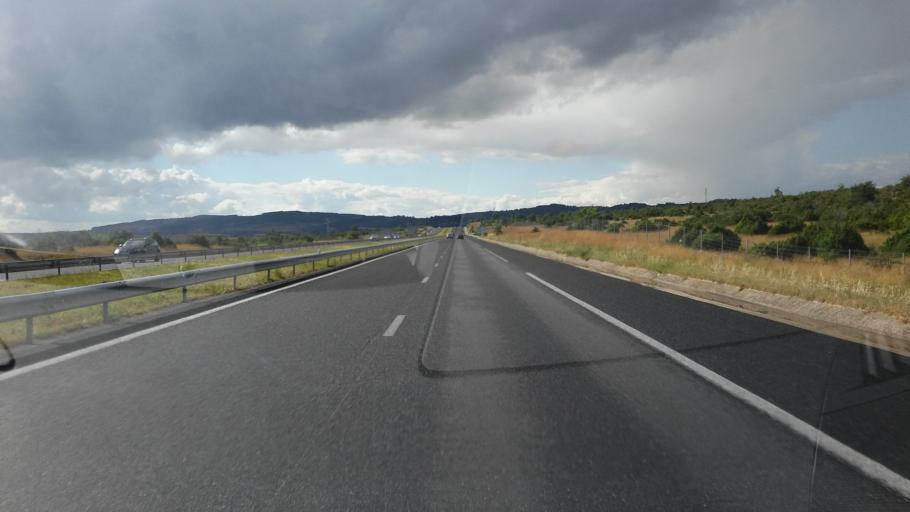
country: FR
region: Midi-Pyrenees
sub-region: Departement de l'Aveyron
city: La Cavalerie
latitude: 43.9373
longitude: 3.2284
